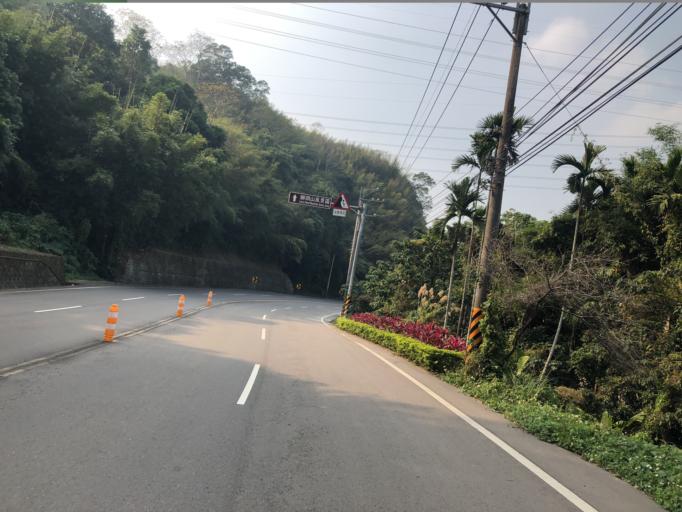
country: TW
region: Taiwan
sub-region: Miaoli
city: Miaoli
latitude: 24.6138
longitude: 120.9571
